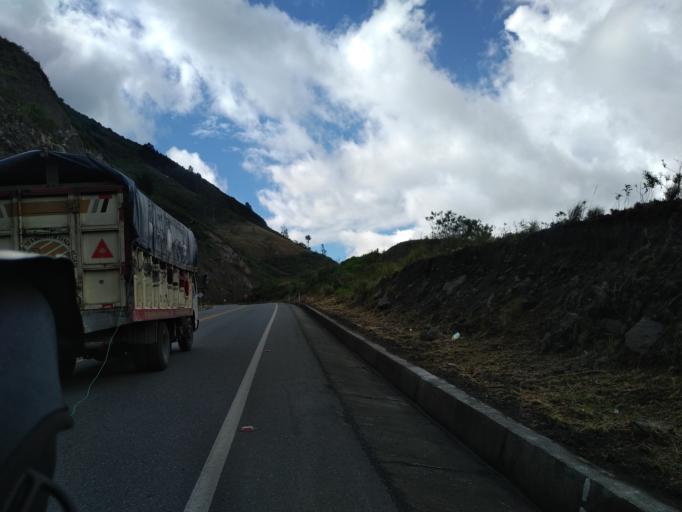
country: EC
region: Tungurahua
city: Banos
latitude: -1.4820
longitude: -78.5185
